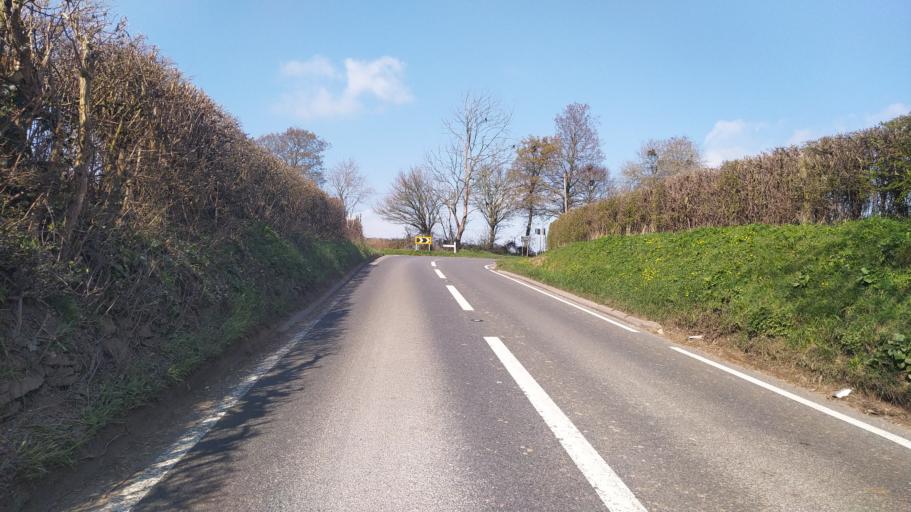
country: GB
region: England
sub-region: Somerset
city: Merriott
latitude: 50.9176
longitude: -2.7743
